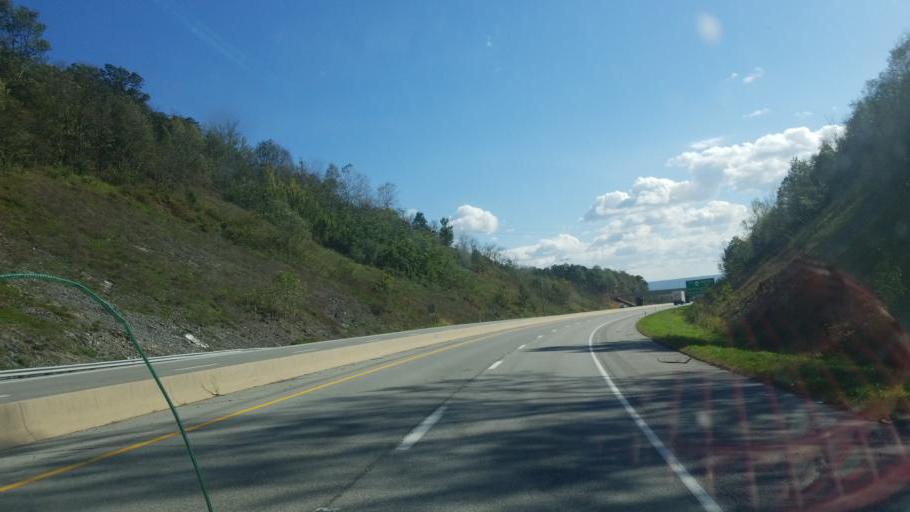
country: US
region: Pennsylvania
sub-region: Bedford County
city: Everett
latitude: 40.0275
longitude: -78.3715
